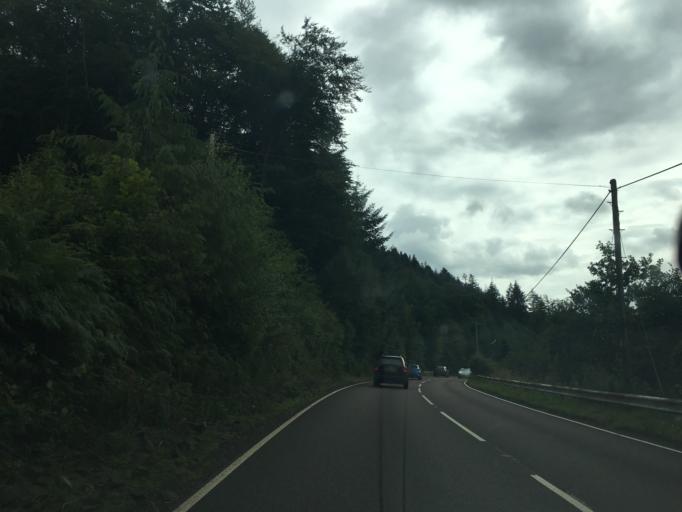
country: GB
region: Scotland
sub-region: Stirling
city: Callander
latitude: 56.2916
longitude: -4.2865
